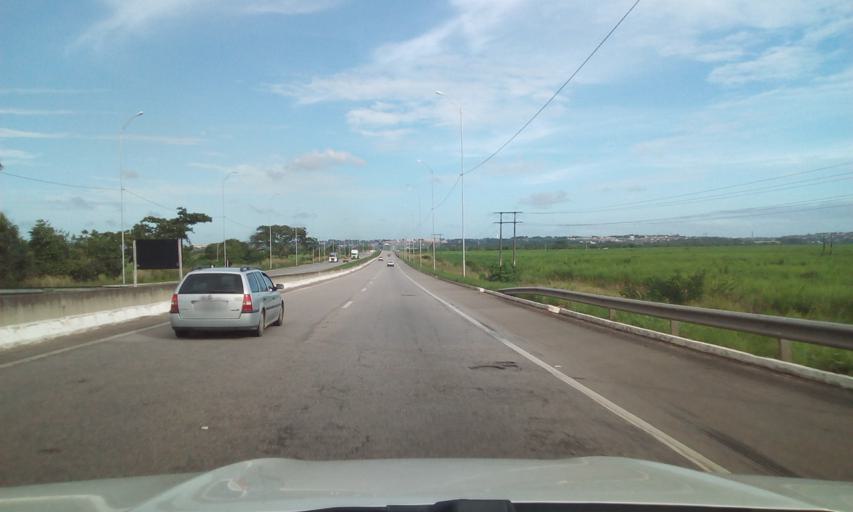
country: BR
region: Paraiba
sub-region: Santa Rita
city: Santa Rita
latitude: -7.0948
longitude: -34.9675
